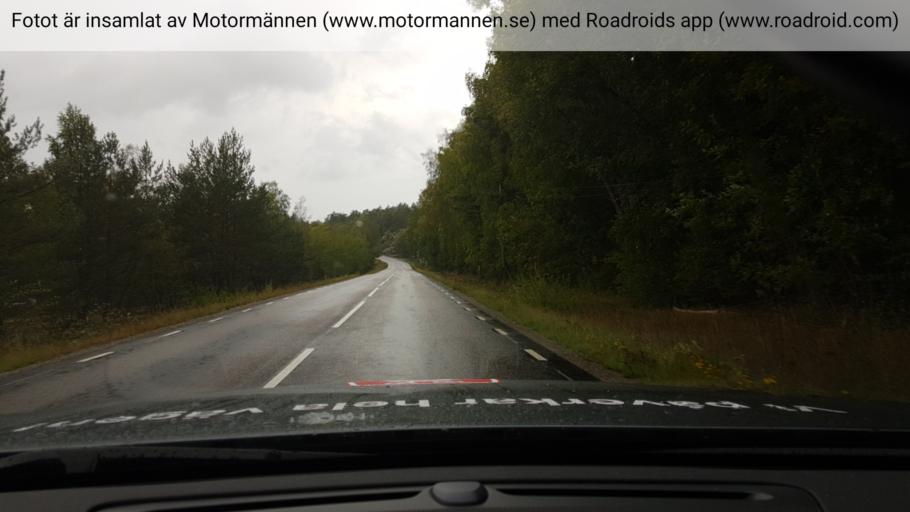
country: SE
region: Stockholm
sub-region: Nynashamns Kommun
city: Nynashamn
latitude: 58.9599
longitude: 18.0218
